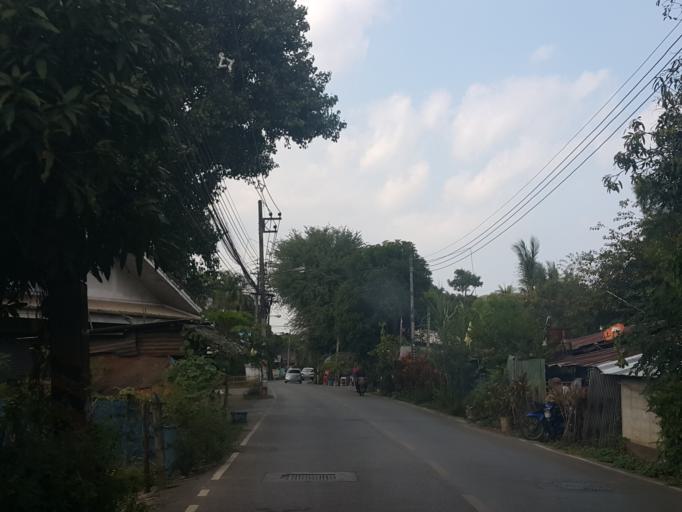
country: TH
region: Chiang Mai
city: Chiang Mai
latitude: 18.8201
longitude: 98.9961
